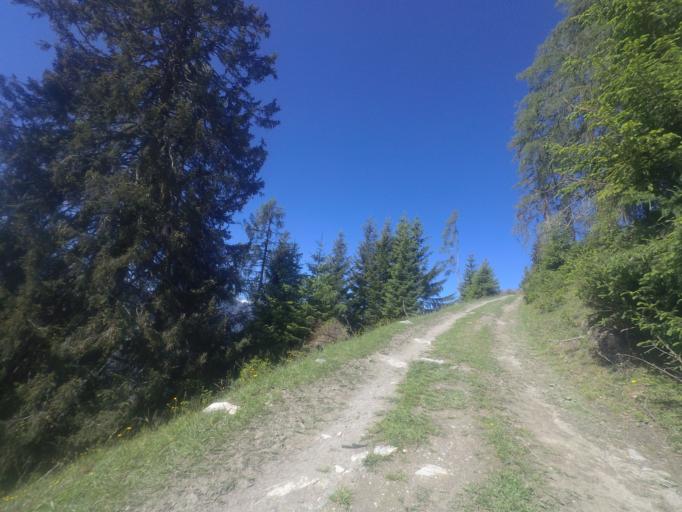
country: AT
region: Salzburg
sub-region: Politischer Bezirk Zell am See
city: Lend
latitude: 47.3225
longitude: 13.0426
